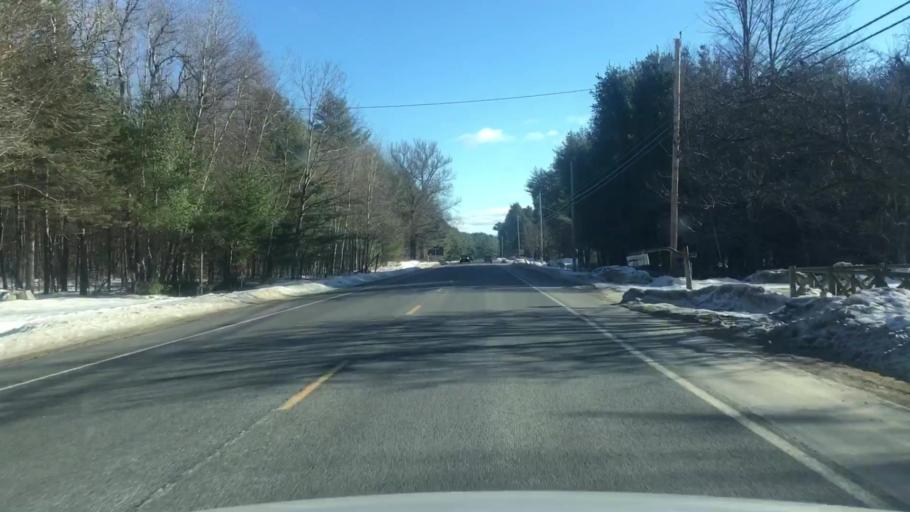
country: US
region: Maine
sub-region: Somerset County
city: Madison
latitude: 44.9416
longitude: -69.8474
